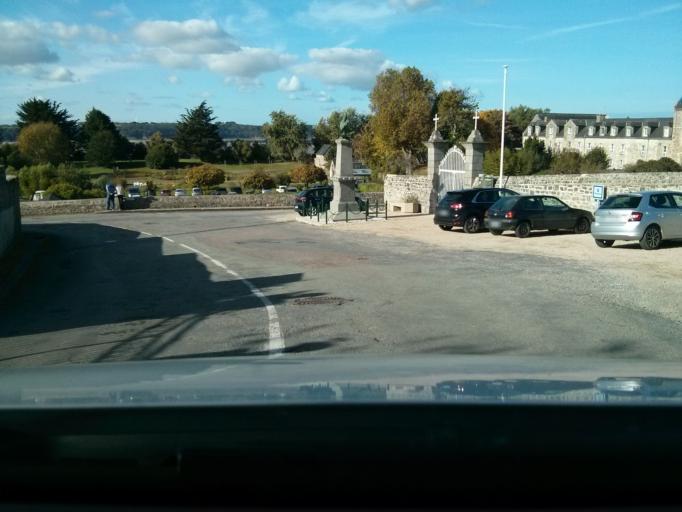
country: FR
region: Brittany
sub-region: Departement des Cotes-d'Armor
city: Lancieux
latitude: 48.6020
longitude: -2.1897
